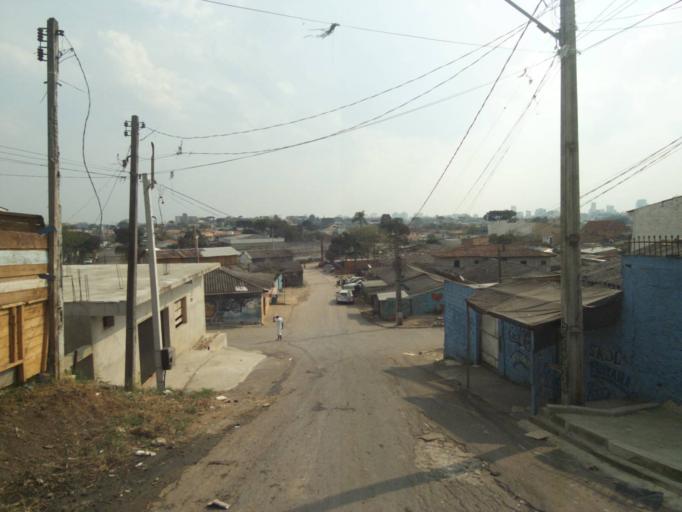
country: BR
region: Parana
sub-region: Curitiba
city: Curitiba
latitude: -25.4629
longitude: -49.2697
